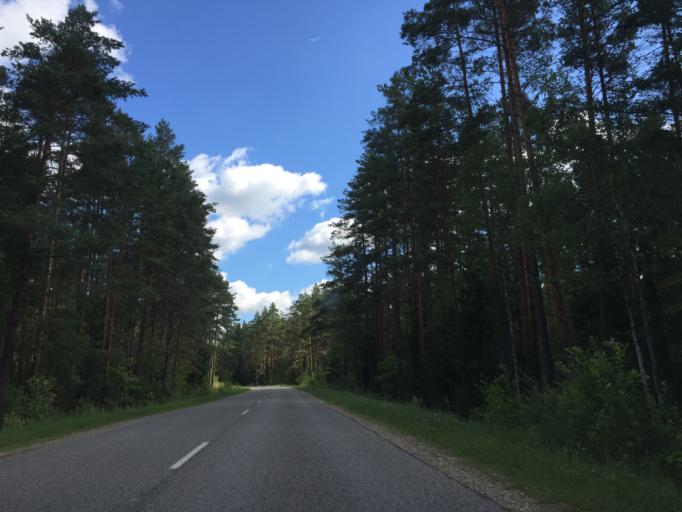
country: LV
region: Garkalne
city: Garkalne
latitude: 56.9645
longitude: 24.4645
